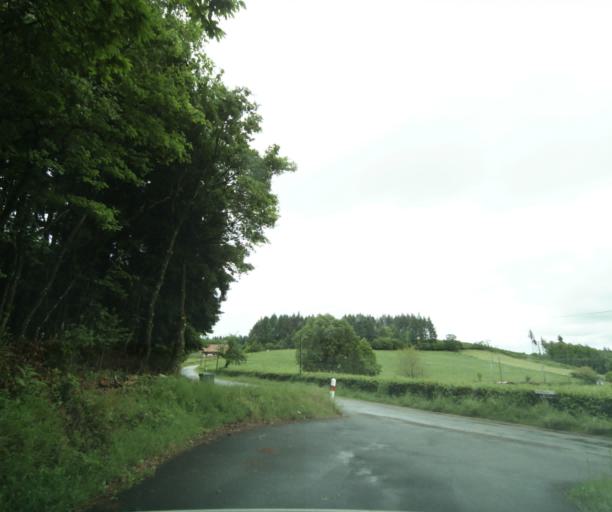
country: FR
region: Bourgogne
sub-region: Departement de Saone-et-Loire
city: Matour
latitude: 46.4450
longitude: 4.4740
